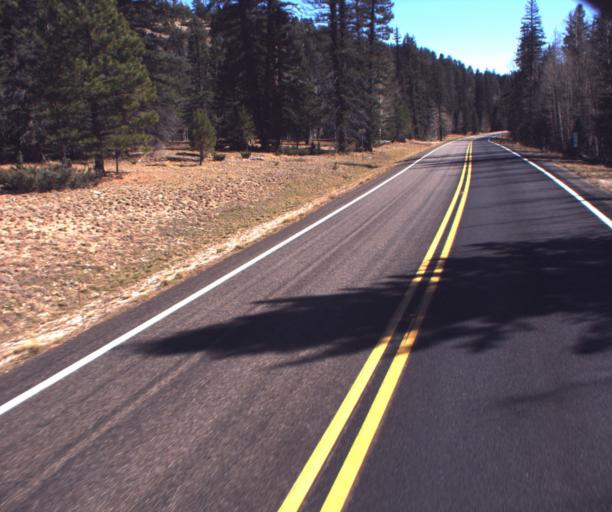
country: US
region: Arizona
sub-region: Coconino County
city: Grand Canyon
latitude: 36.5252
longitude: -112.1462
